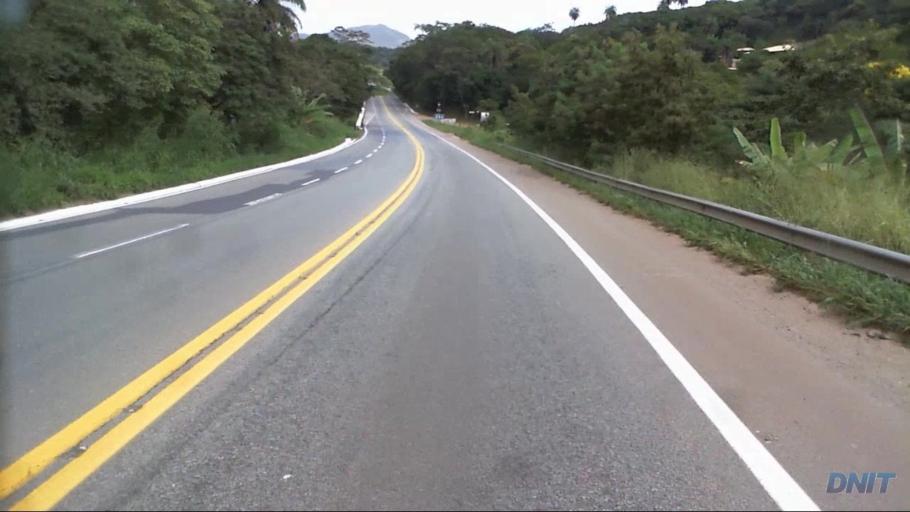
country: BR
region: Minas Gerais
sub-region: Santa Luzia
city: Santa Luzia
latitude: -19.7937
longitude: -43.7468
